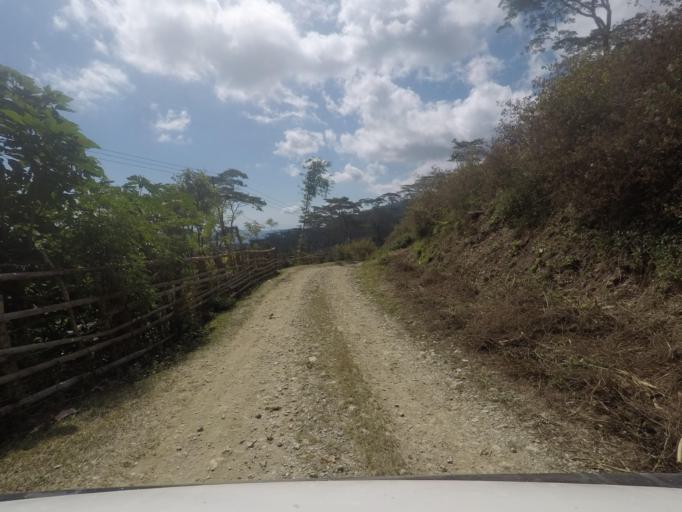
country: TL
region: Ermera
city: Gleno
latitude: -8.7506
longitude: 125.3257
